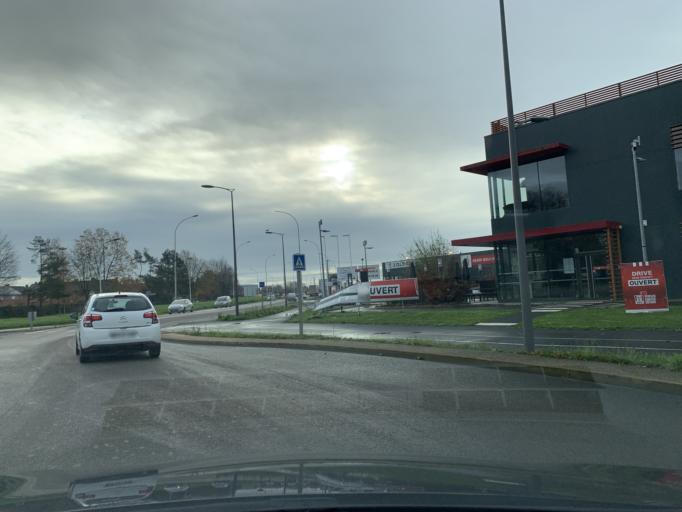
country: FR
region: Nord-Pas-de-Calais
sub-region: Departement du Nord
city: Dechy
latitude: 50.3440
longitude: 3.0929
